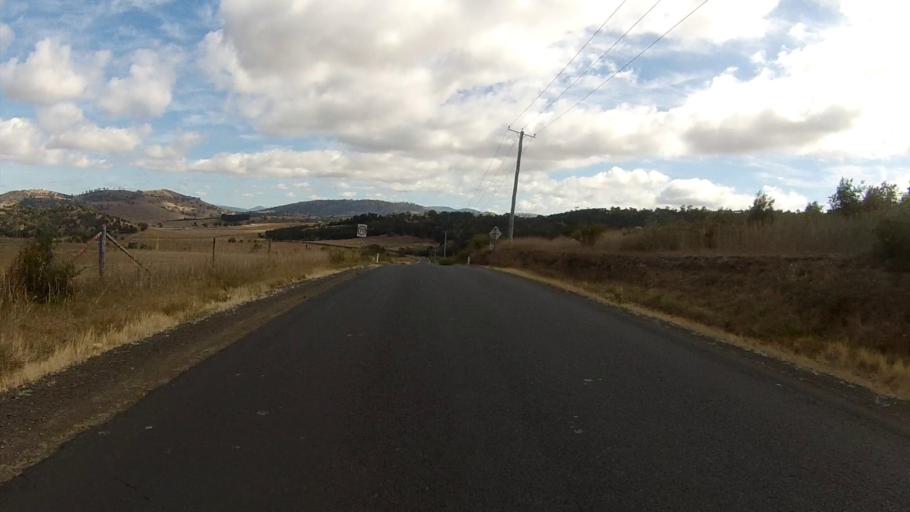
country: AU
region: Tasmania
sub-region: Brighton
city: Old Beach
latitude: -42.7578
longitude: 147.3046
